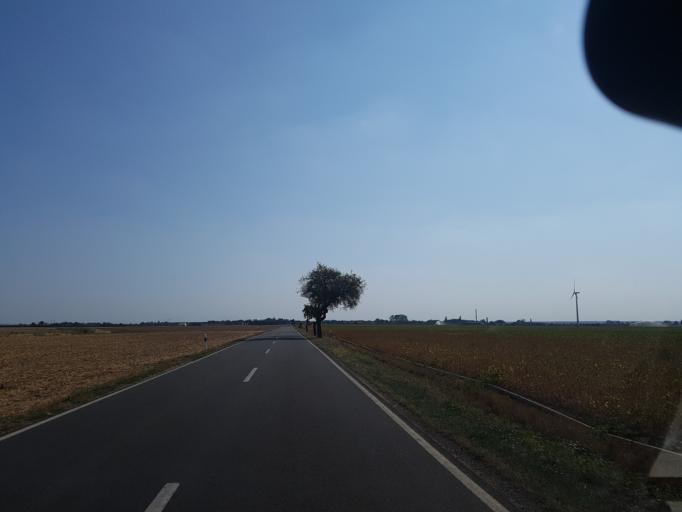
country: DE
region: Saxony-Anhalt
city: Prettin
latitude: 51.6616
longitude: 12.9900
